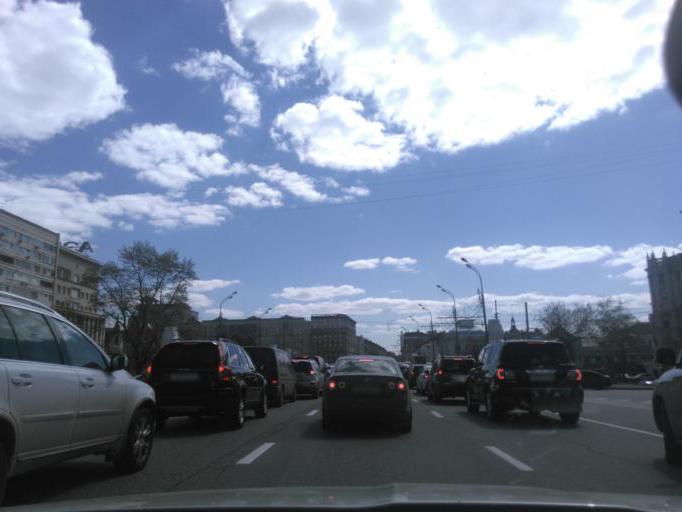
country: RU
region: Moskovskaya
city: Dorogomilovo
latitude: 55.7789
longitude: 37.5799
